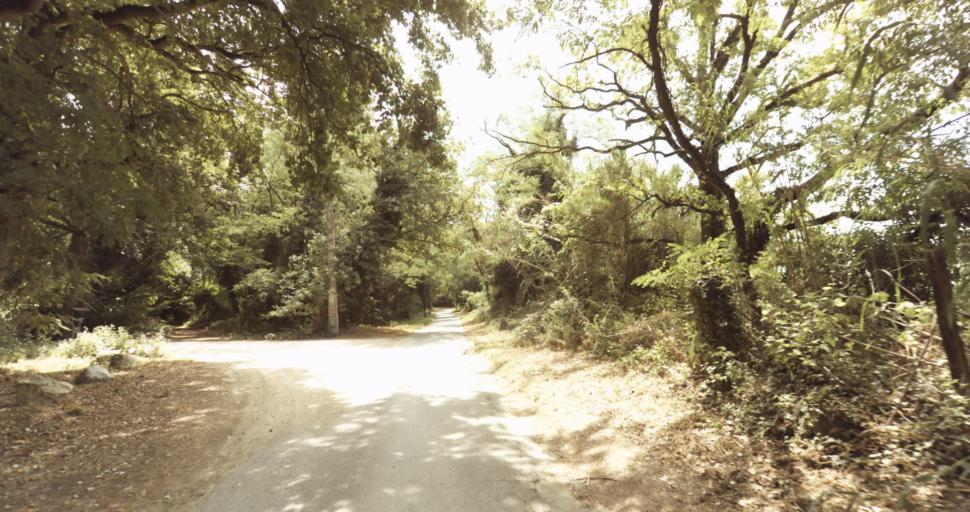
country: FR
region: Provence-Alpes-Cote d'Azur
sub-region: Departement du Vaucluse
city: Loriol-du-Comtat
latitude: 44.0583
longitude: 4.9855
